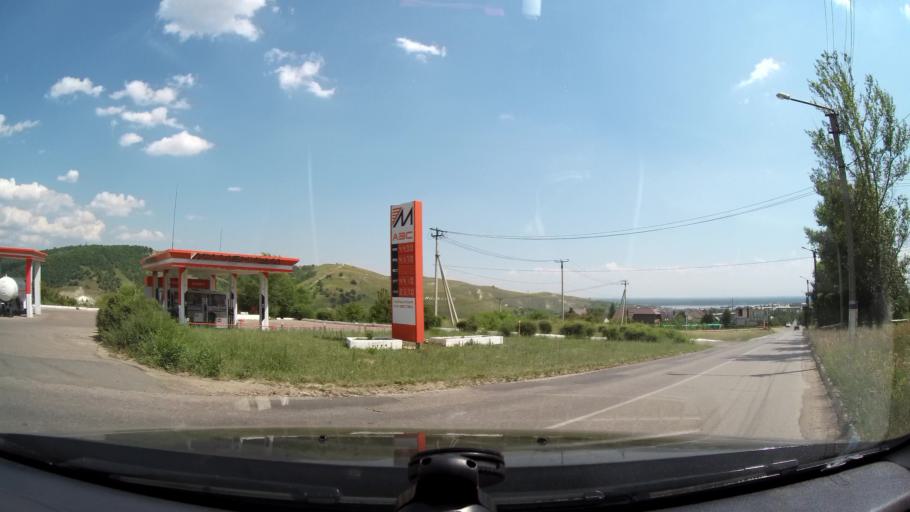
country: RU
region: Saratov
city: Vol'sk
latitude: 52.0659
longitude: 47.3770
